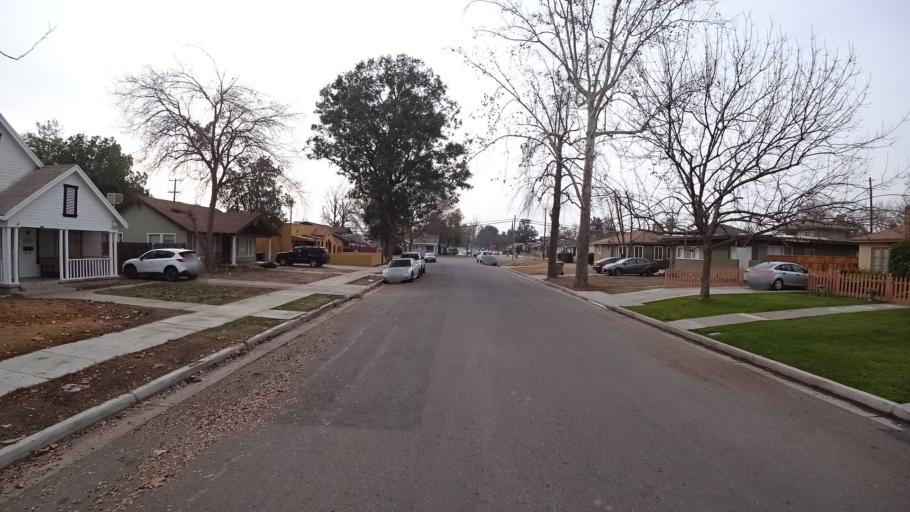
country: US
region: California
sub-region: Kern County
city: Bakersfield
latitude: 35.3620
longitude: -119.0233
